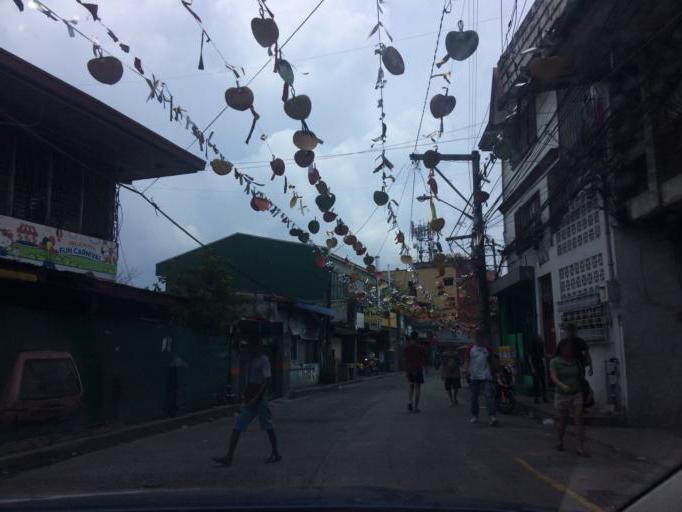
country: PH
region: Metro Manila
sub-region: Makati City
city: Makati City
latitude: 14.5482
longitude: 121.0039
